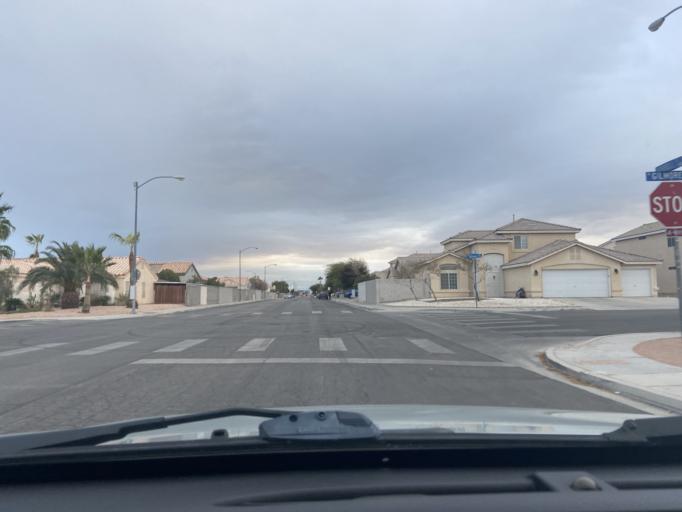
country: US
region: Nevada
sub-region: Clark County
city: Las Vegas
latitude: 36.2286
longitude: -115.1846
